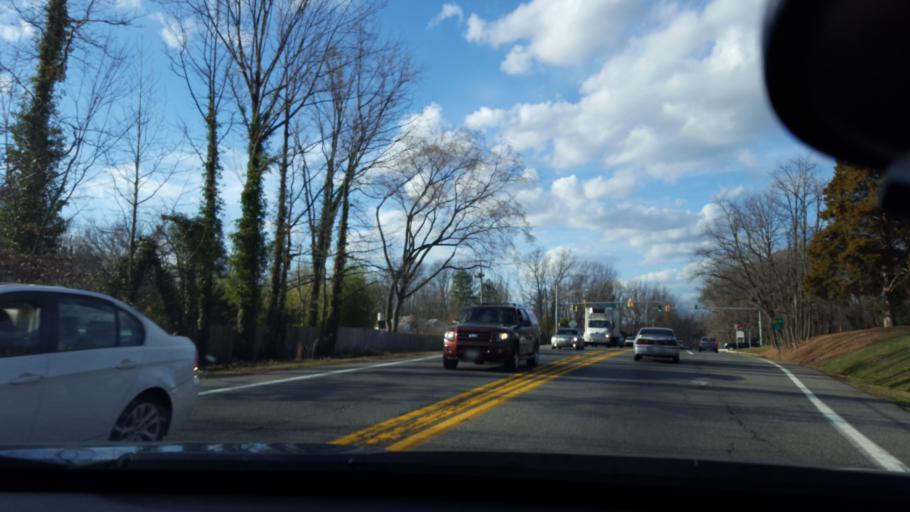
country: US
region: Maryland
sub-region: Prince George's County
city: Bowie
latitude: 38.9675
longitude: -76.7542
